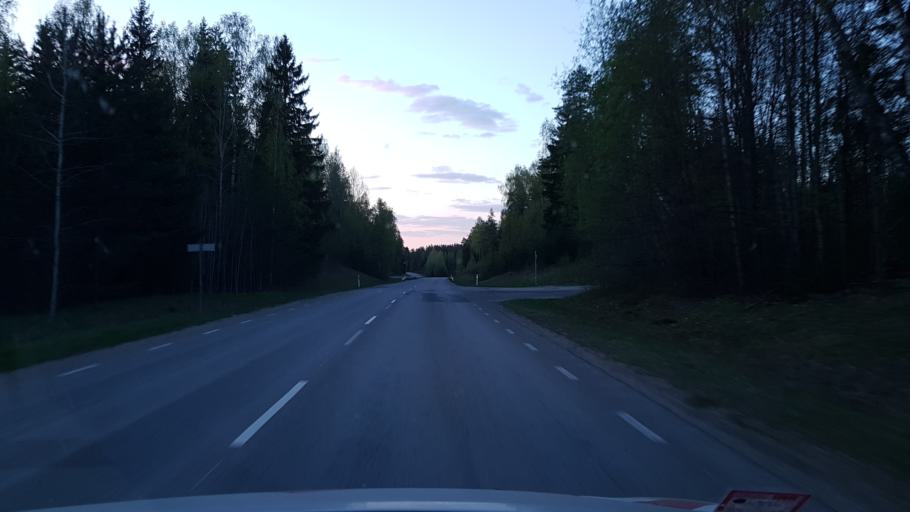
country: EE
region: Vorumaa
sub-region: Voru linn
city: Voru
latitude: 57.7987
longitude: 27.0339
